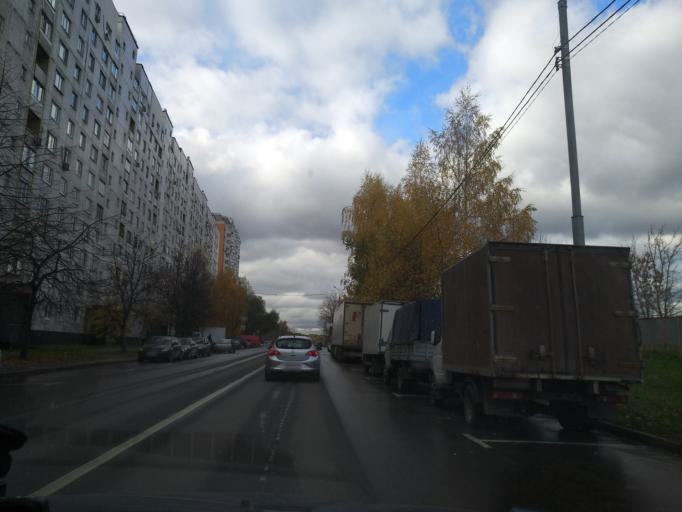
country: RU
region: Moscow
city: Bibirevo
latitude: 55.9004
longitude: 37.6173
